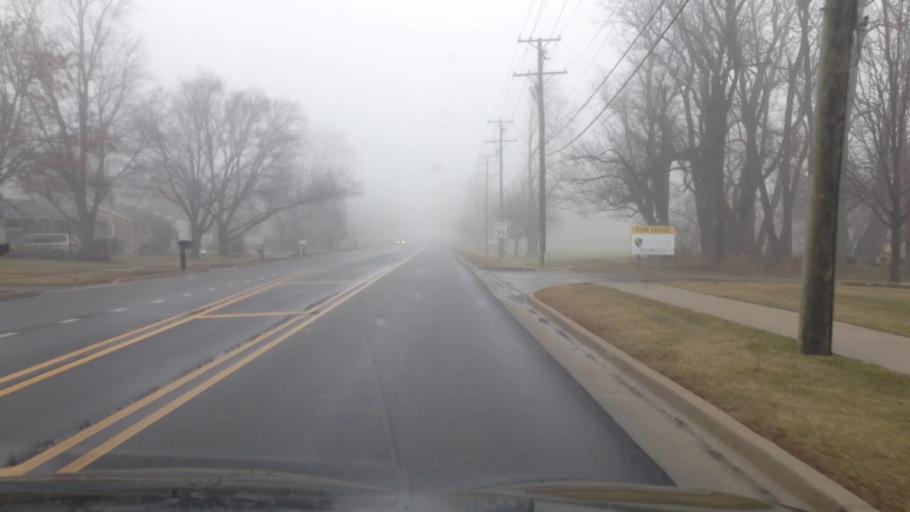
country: US
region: Illinois
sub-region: McHenry County
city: Woodstock
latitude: 42.3289
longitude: -88.4431
